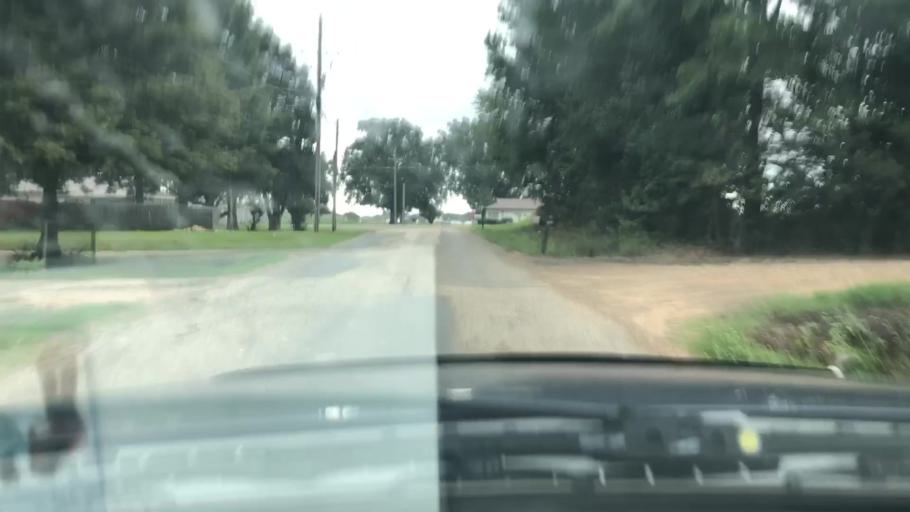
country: US
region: Texas
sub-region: Bowie County
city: Wake Village
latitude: 33.3759
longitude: -94.0934
